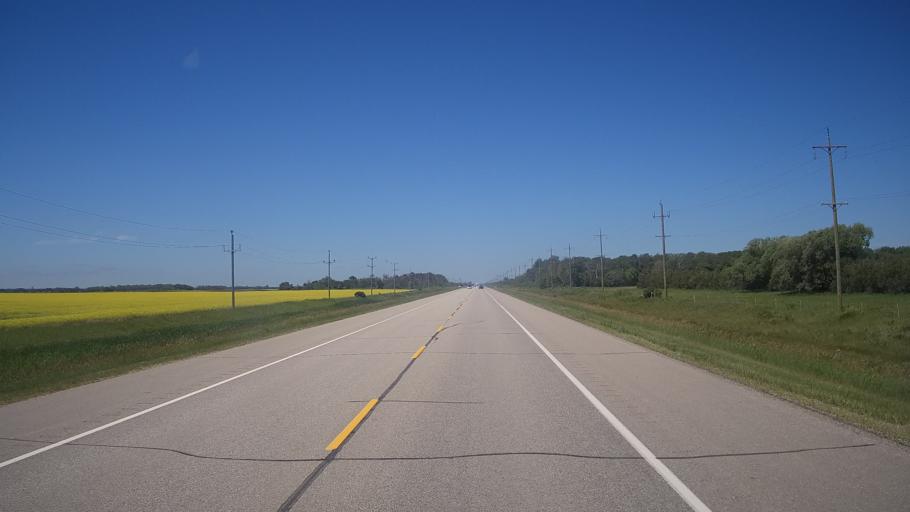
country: CA
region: Manitoba
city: Neepawa
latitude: 50.2257
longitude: -99.0918
